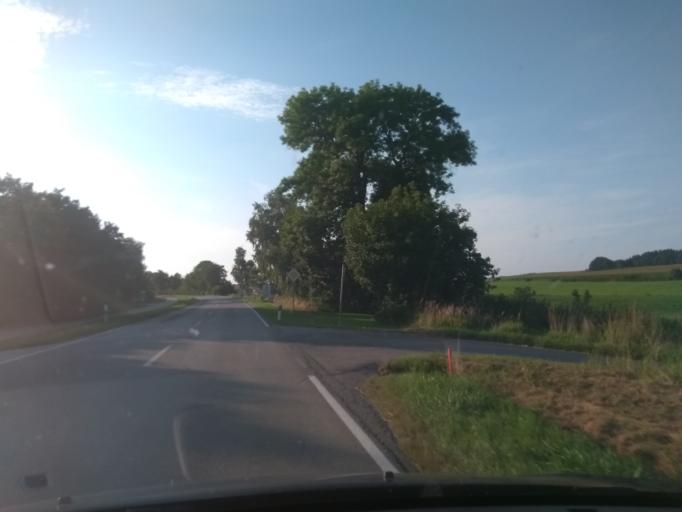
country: DE
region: Bavaria
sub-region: Upper Bavaria
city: Markt Indersdorf
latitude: 48.3771
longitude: 11.3598
